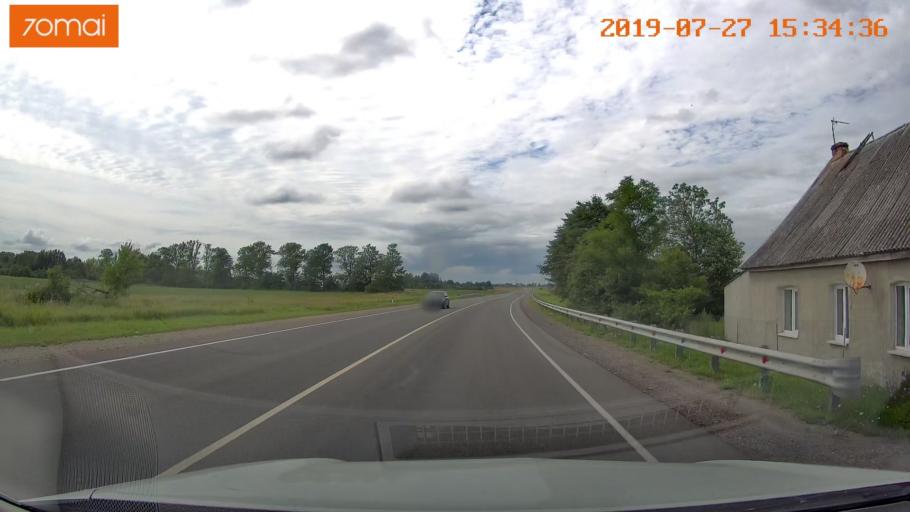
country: RU
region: Kaliningrad
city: Nesterov
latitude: 54.6119
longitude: 22.4198
